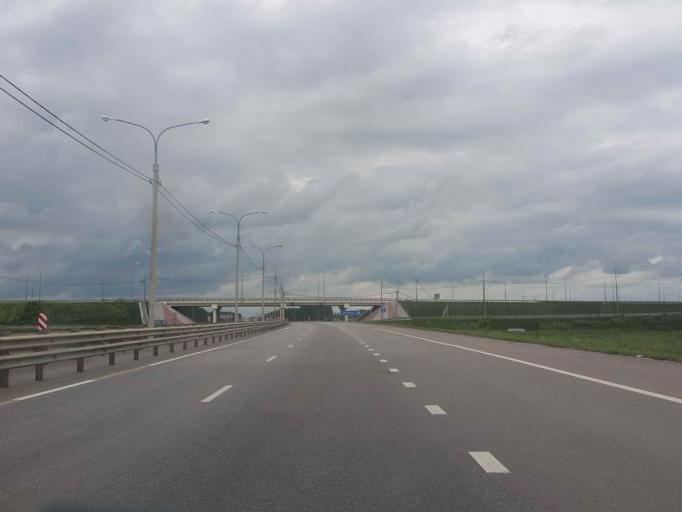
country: RU
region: Tambov
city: Zavoronezhskoye
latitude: 52.8551
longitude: 40.7795
